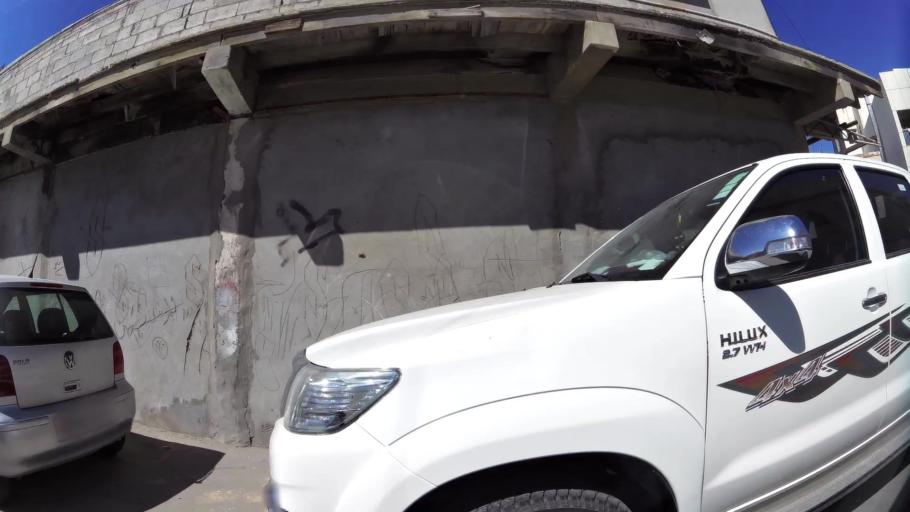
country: BH
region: Muharraq
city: Al Muharraq
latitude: 26.2439
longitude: 50.6148
